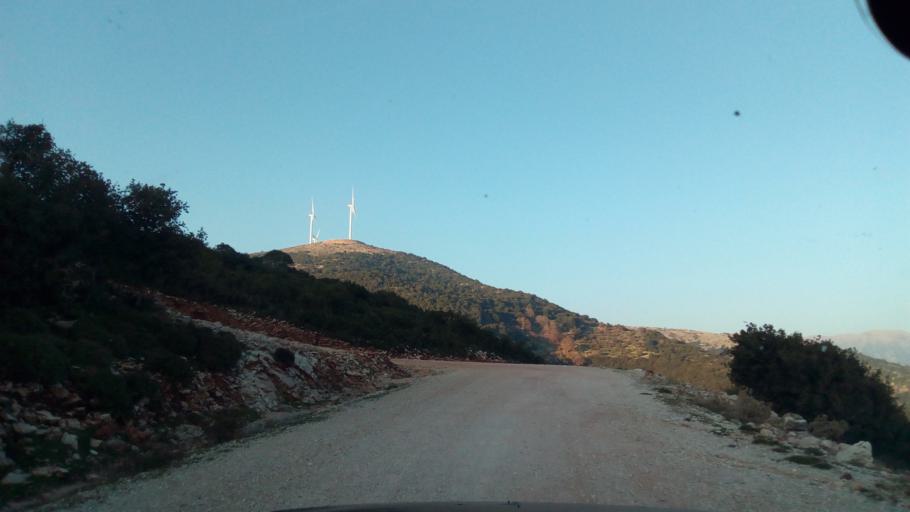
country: GR
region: West Greece
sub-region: Nomos Aitolias kai Akarnanias
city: Nafpaktos
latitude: 38.4348
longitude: 21.8522
